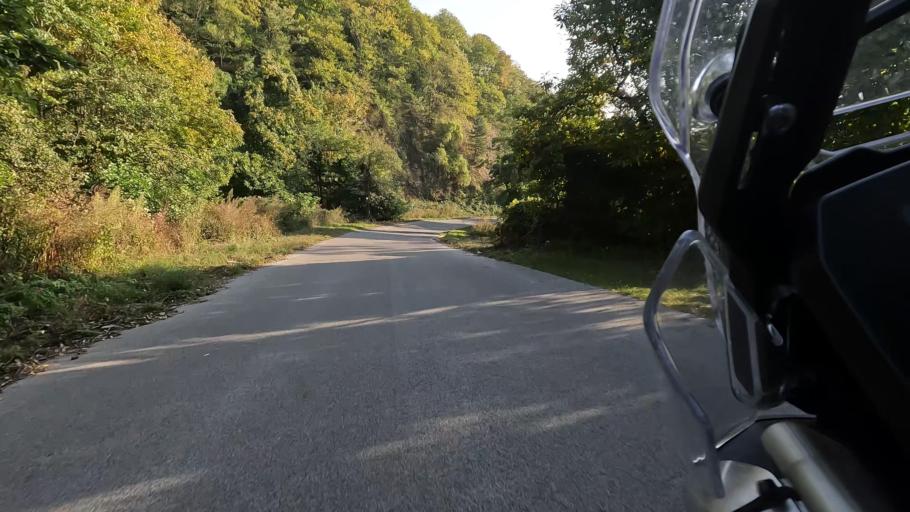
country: IT
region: Liguria
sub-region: Provincia di Savona
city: San Giovanni
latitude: 44.4175
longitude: 8.5298
